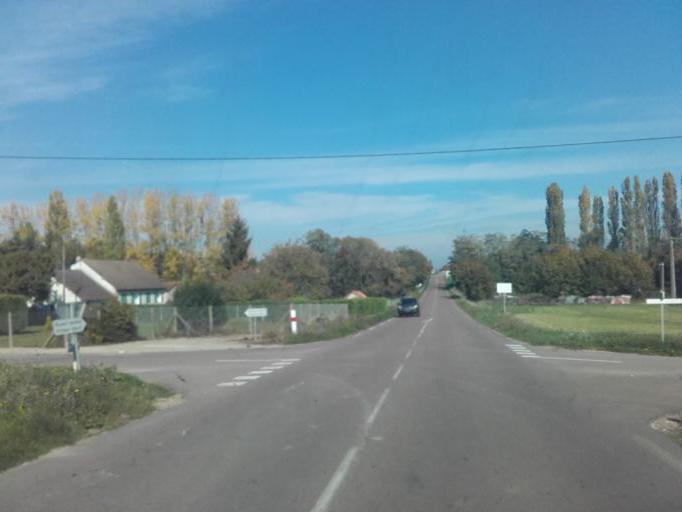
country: FR
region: Bourgogne
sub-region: Departement de Saone-et-Loire
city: Rully
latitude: 46.8748
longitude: 4.7524
